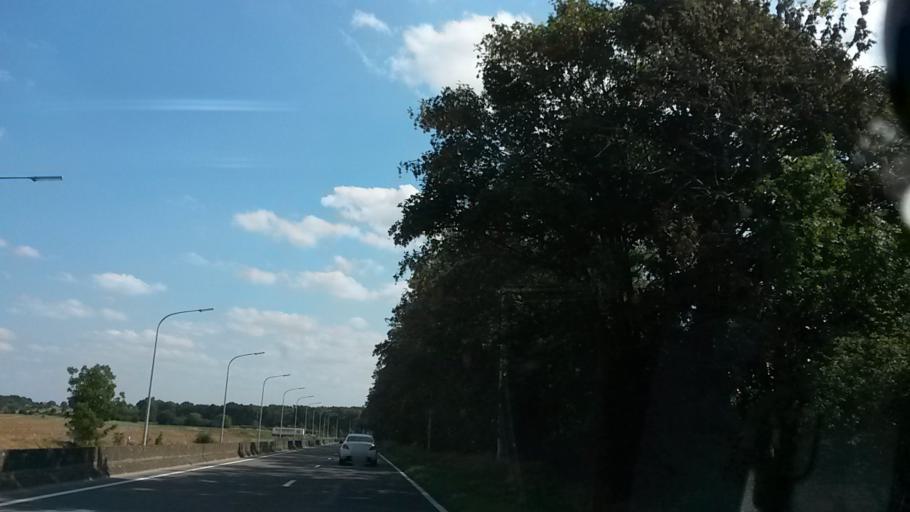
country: BE
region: Wallonia
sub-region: Province de Namur
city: Floreffe
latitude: 50.4266
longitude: 4.7298
